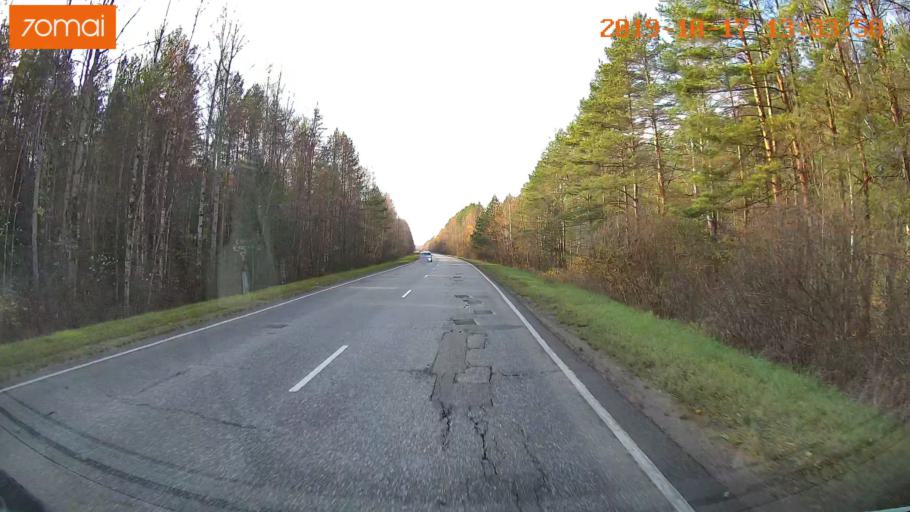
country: RU
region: Vladimir
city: Velikodvorskiy
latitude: 55.1445
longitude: 40.7281
